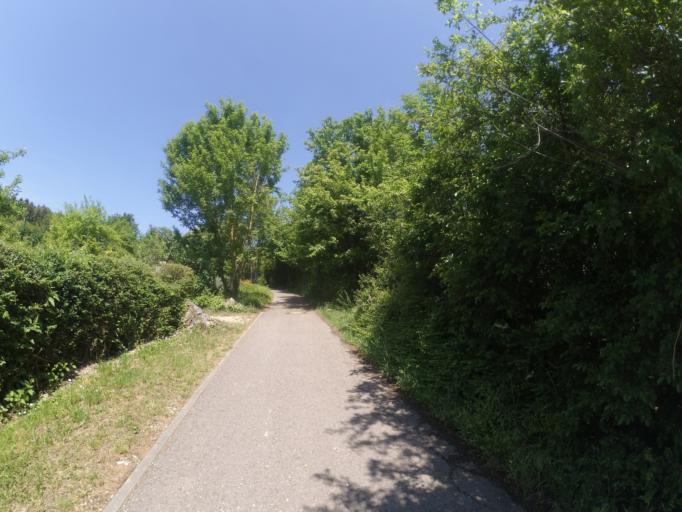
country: DE
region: Baden-Wuerttemberg
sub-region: Tuebingen Region
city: Ulm
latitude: 48.4176
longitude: 9.9678
